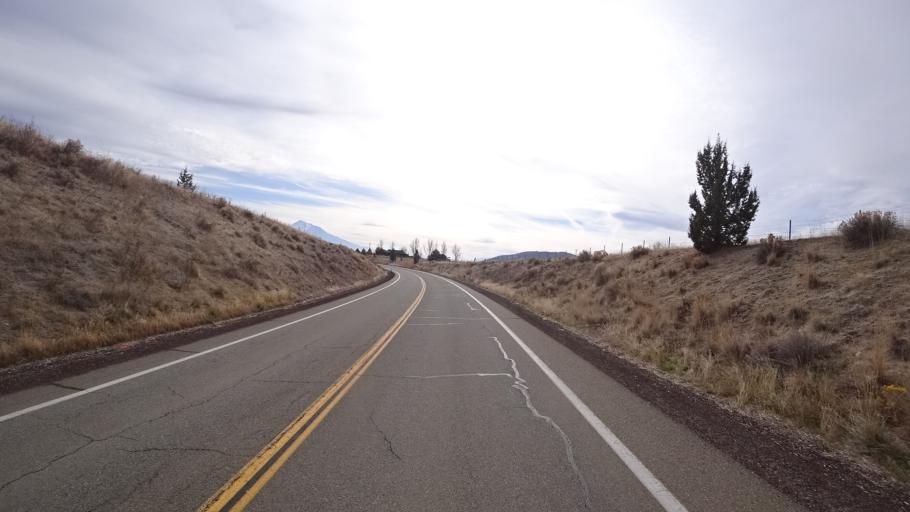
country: US
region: California
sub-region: Siskiyou County
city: Montague
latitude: 41.7026
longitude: -122.5396
